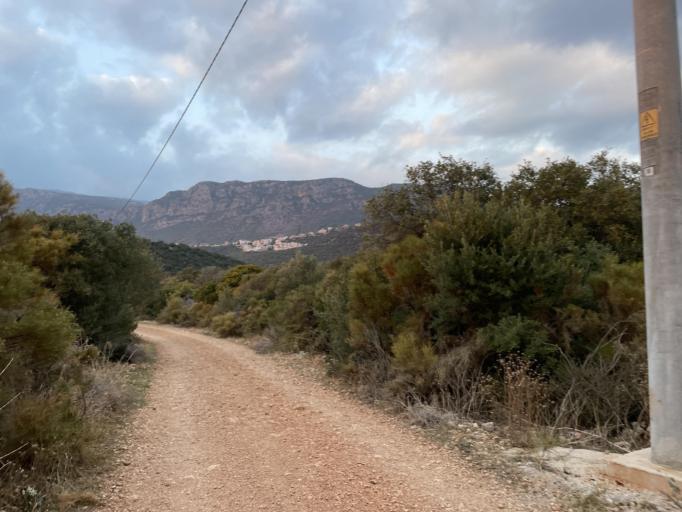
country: TR
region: Antalya
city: Kas
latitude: 36.1838
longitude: 29.6527
